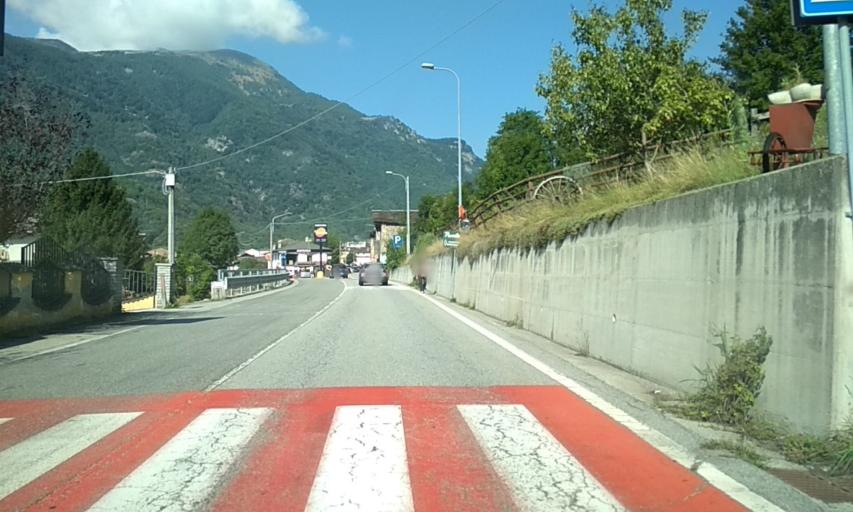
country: IT
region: Piedmont
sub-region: Provincia di Torino
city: Locana
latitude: 45.4163
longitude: 7.4656
